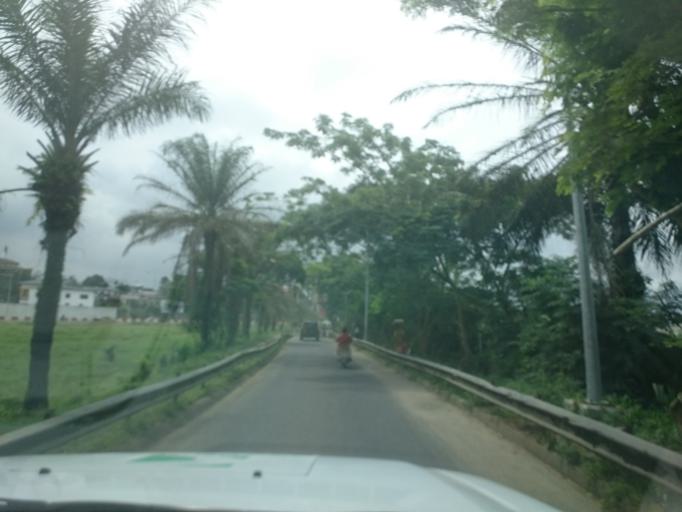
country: CM
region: Littoral
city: Douala
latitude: 4.0156
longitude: 9.6998
